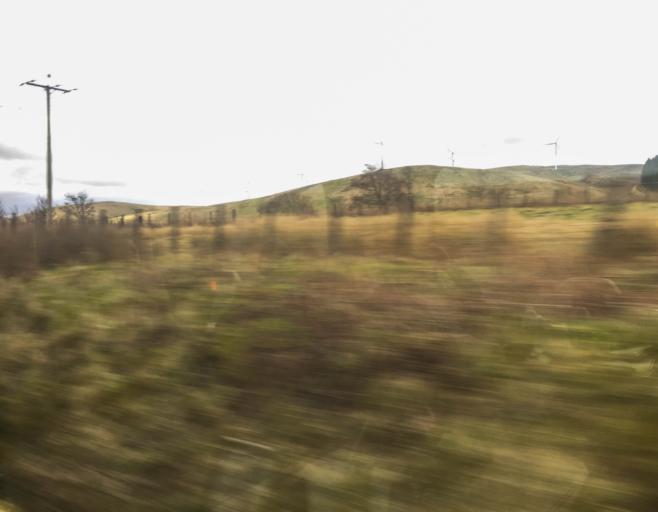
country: GB
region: Scotland
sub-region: South Lanarkshire
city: Biggar
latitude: 55.4504
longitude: -3.6530
